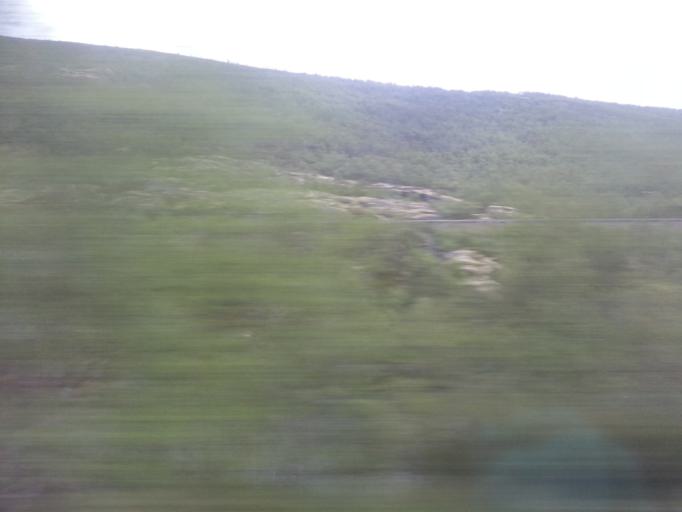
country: NO
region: Sor-Trondelag
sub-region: Oppdal
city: Oppdal
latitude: 62.3133
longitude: 9.6119
